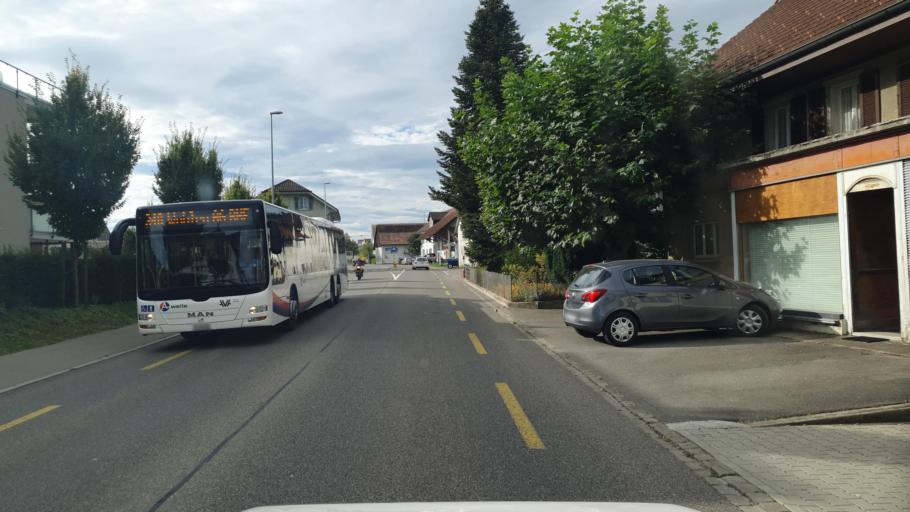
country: CH
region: Aargau
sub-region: Bezirk Bremgarten
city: Sarmenstorf
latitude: 47.2971
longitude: 8.2436
